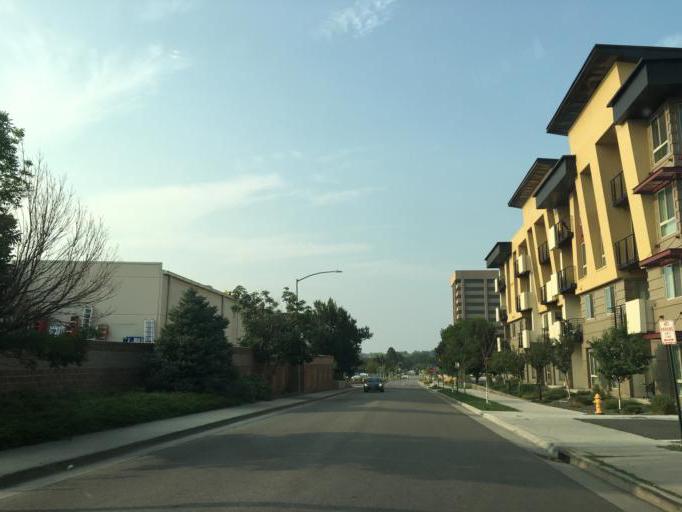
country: US
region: Colorado
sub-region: Arapahoe County
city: Glendale
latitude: 39.7011
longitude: -104.9364
